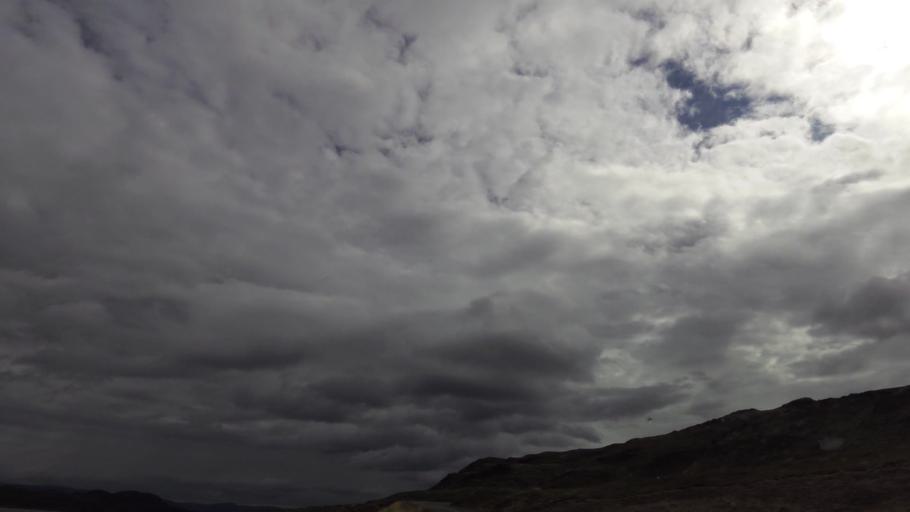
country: IS
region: West
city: Stykkisholmur
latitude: 65.5275
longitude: -22.1227
